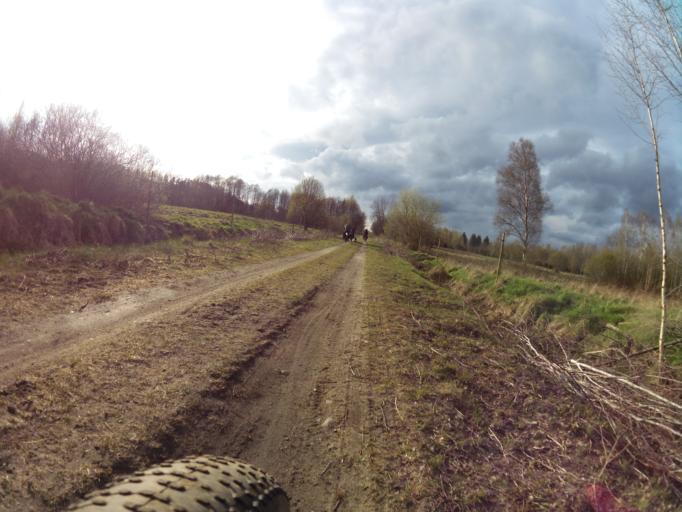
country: PL
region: West Pomeranian Voivodeship
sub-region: Powiat slawienski
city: Slawno
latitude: 54.3343
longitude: 16.7201
